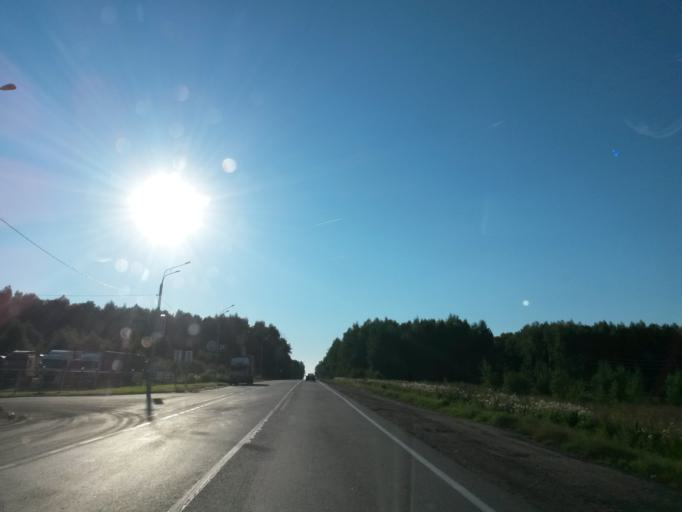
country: RU
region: Jaroslavl
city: Gavrilov-Yam
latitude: 57.2707
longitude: 39.9593
